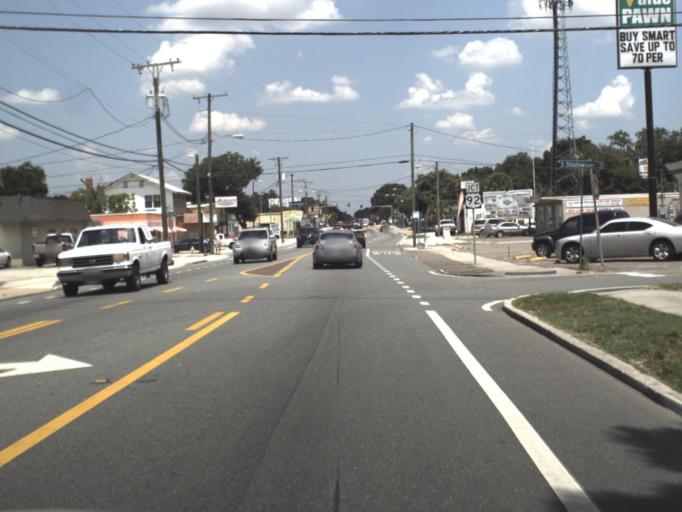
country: US
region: Florida
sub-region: Hillsborough County
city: Tampa
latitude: 27.9936
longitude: -82.4511
